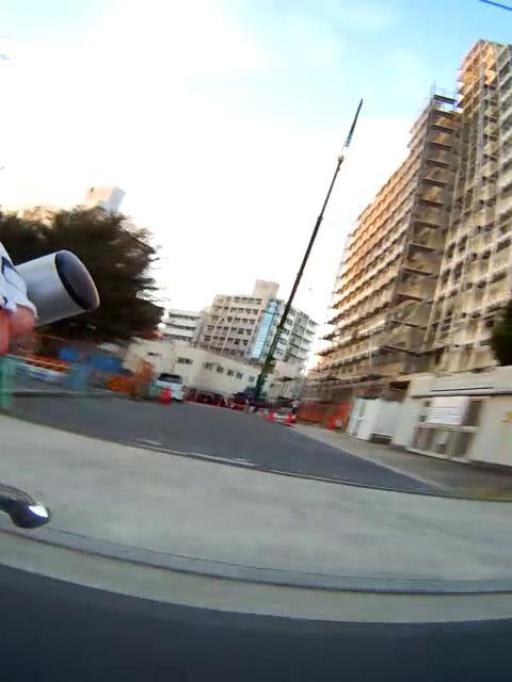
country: JP
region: Osaka
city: Osaka-shi
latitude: 34.7275
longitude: 135.5060
